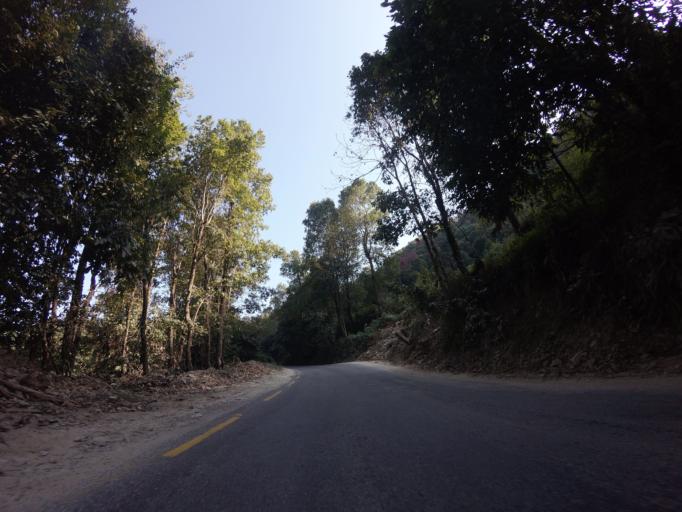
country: NP
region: Western Region
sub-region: Gandaki Zone
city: Pokhara
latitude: 28.1881
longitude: 83.9012
